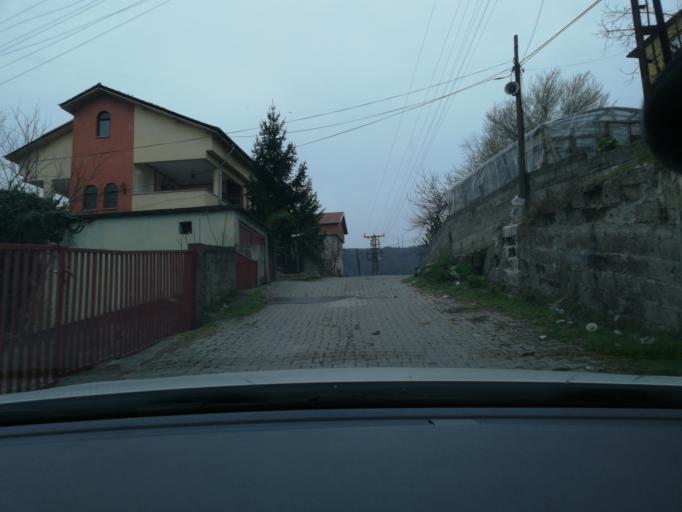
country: TR
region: Zonguldak
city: Saltukova
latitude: 41.5175
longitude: 32.0686
